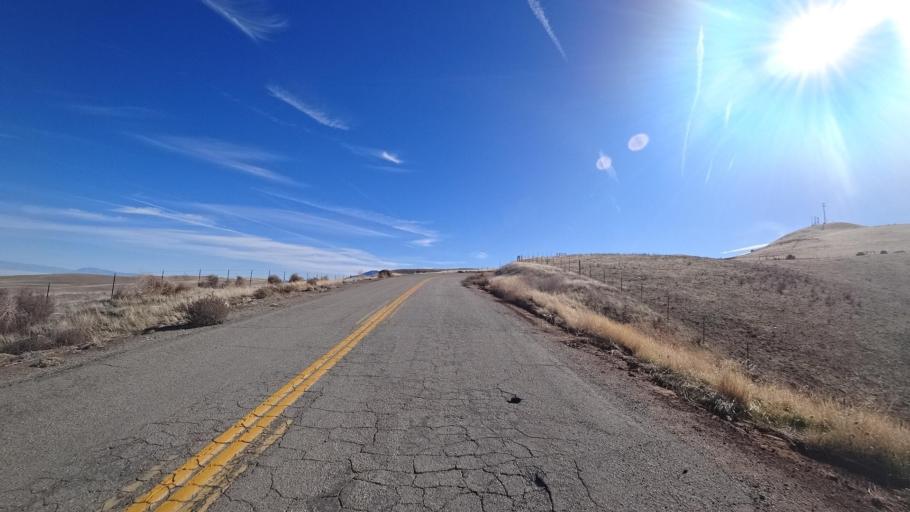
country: US
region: California
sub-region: Kern County
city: Maricopa
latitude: 34.9290
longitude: -119.4075
